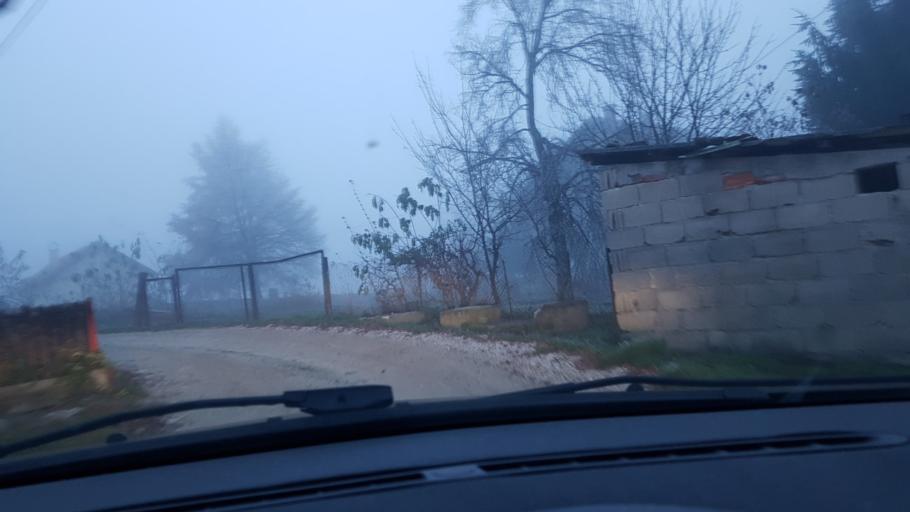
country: HR
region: Krapinsko-Zagorska
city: Pregrada
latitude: 46.2007
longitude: 15.7482
